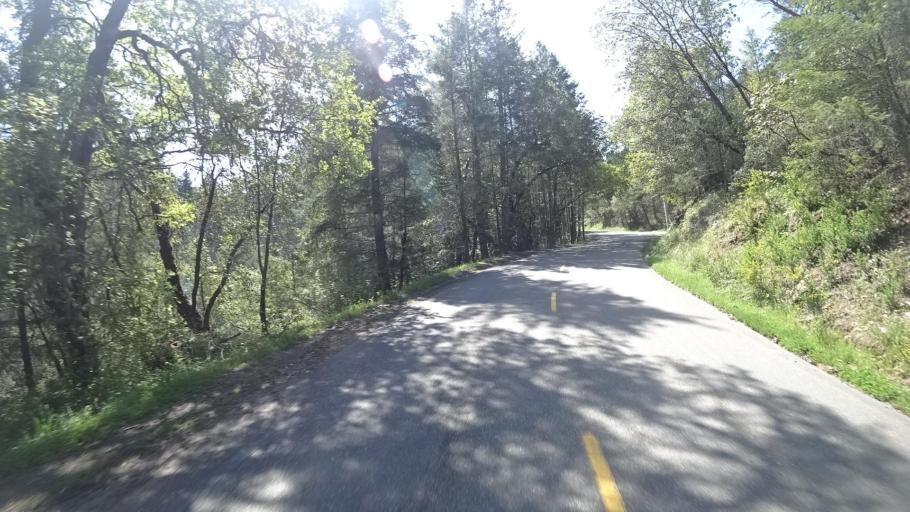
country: US
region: California
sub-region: Humboldt County
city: Redway
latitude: 40.1383
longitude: -123.6293
